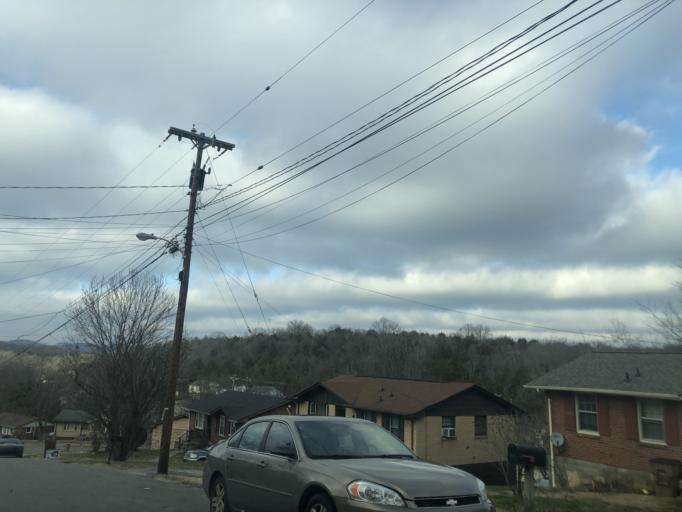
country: US
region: Tennessee
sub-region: Davidson County
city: Nashville
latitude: 36.2155
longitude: -86.7899
